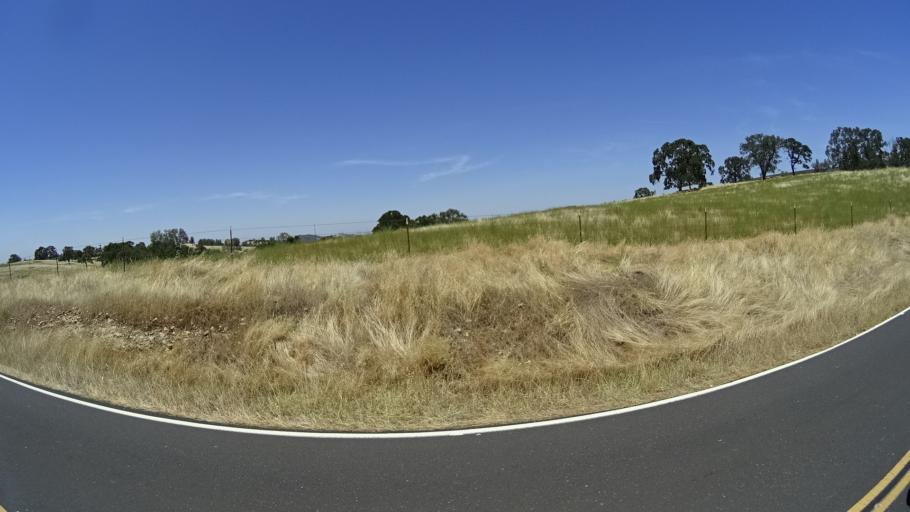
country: US
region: California
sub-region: Calaveras County
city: Valley Springs
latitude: 38.2291
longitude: -120.8179
